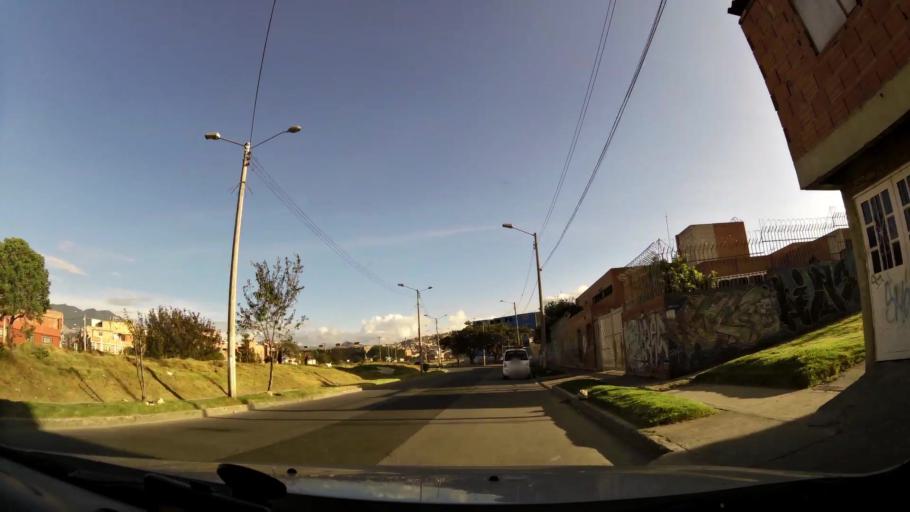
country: CO
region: Cundinamarca
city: Soacha
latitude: 4.5717
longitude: -74.1481
